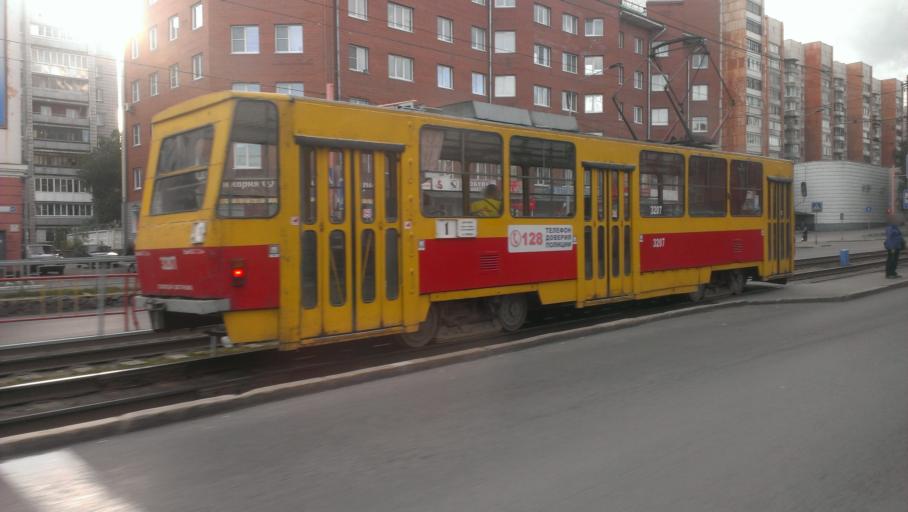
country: RU
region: Altai Krai
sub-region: Gorod Barnaulskiy
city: Barnaul
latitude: 53.3424
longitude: 83.7693
